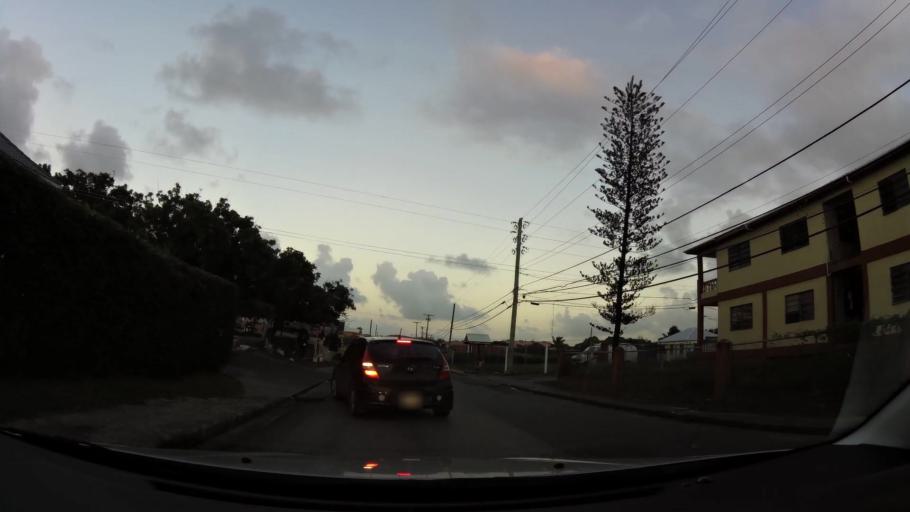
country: AG
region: Saint John
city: Saint John's
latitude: 17.1243
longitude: -61.8302
